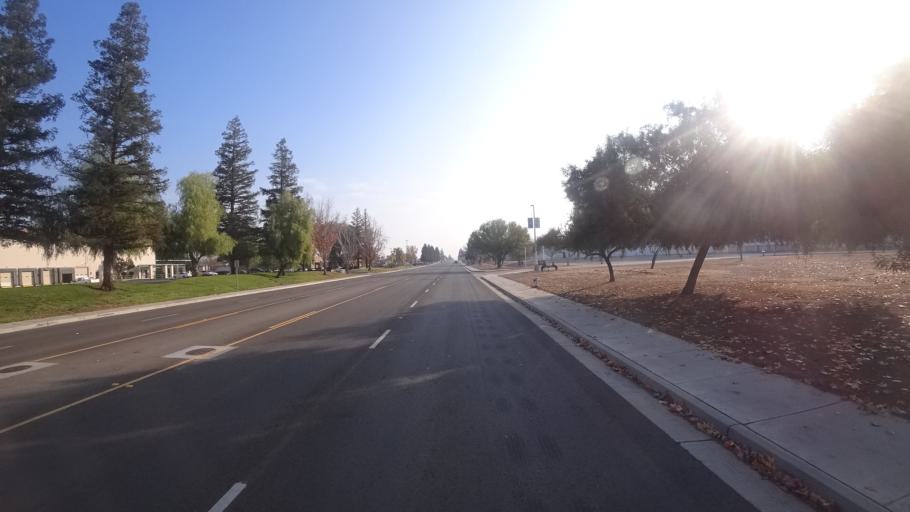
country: US
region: California
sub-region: Kern County
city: Greenacres
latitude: 35.3131
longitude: -119.0873
